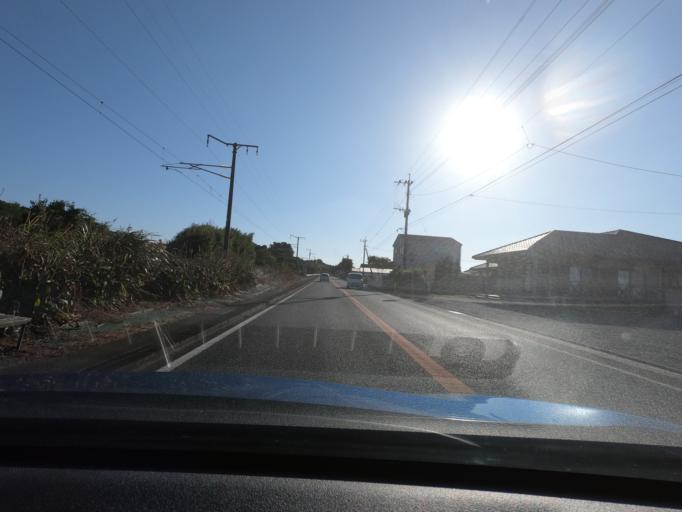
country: JP
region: Kagoshima
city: Izumi
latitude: 32.1395
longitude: 130.3541
